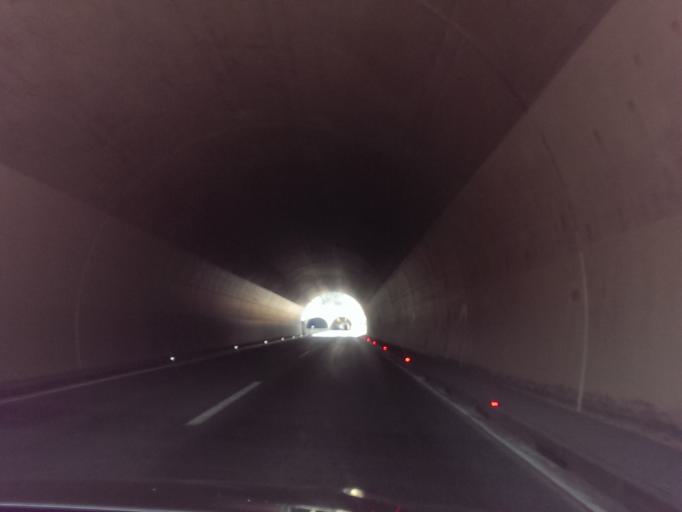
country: AT
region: Upper Austria
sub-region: Politischer Bezirk Kirchdorf an der Krems
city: Rossleithen
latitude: 47.7646
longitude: 14.1970
